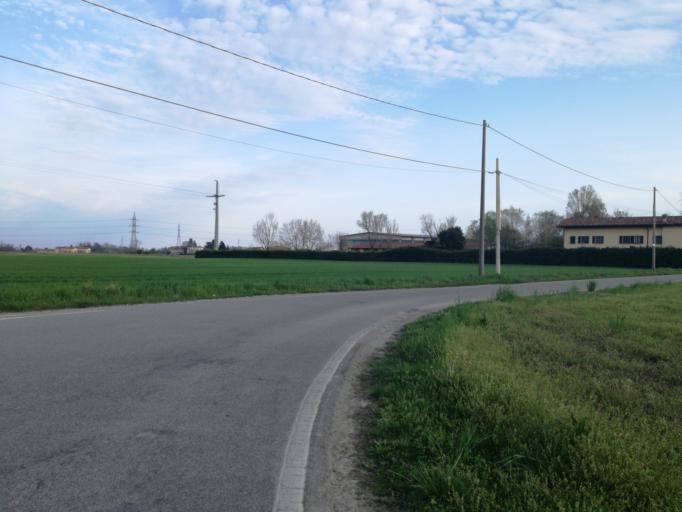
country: IT
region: Lombardy
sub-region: Provincia di Monza e Brianza
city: Porto d'Adda
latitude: 45.6681
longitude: 9.4611
